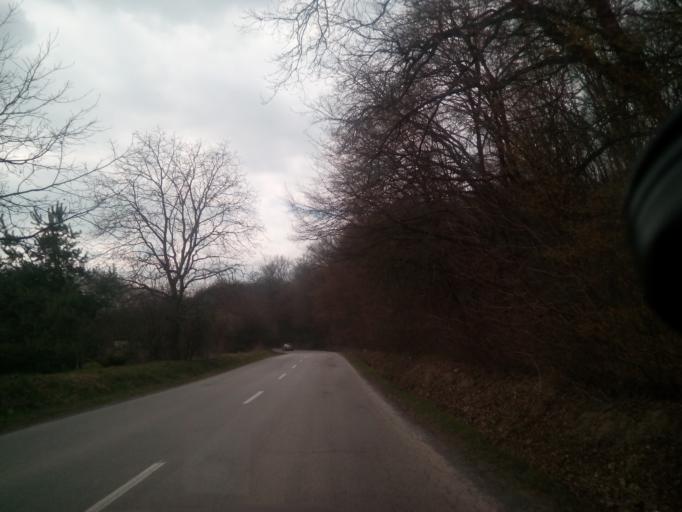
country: SK
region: Kosicky
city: Kosice
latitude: 48.7127
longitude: 21.3195
